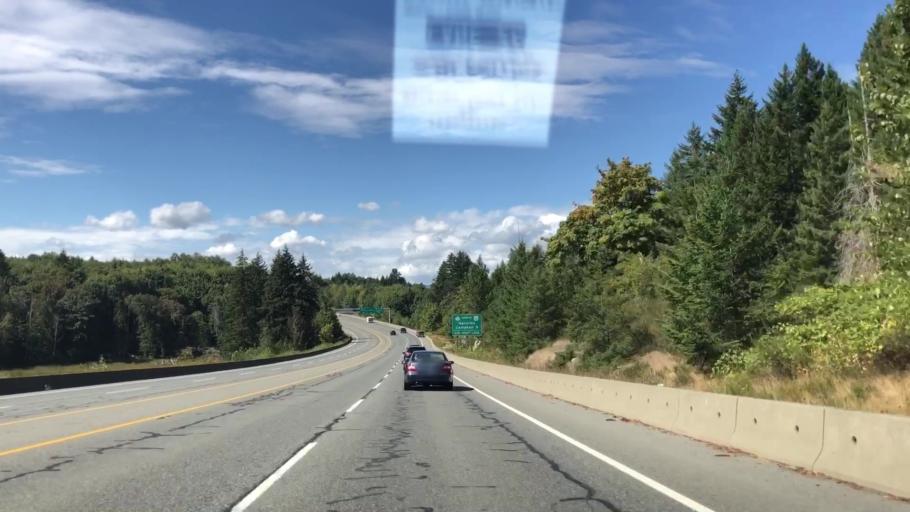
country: CA
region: British Columbia
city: Nanaimo
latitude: 49.1136
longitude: -123.8841
